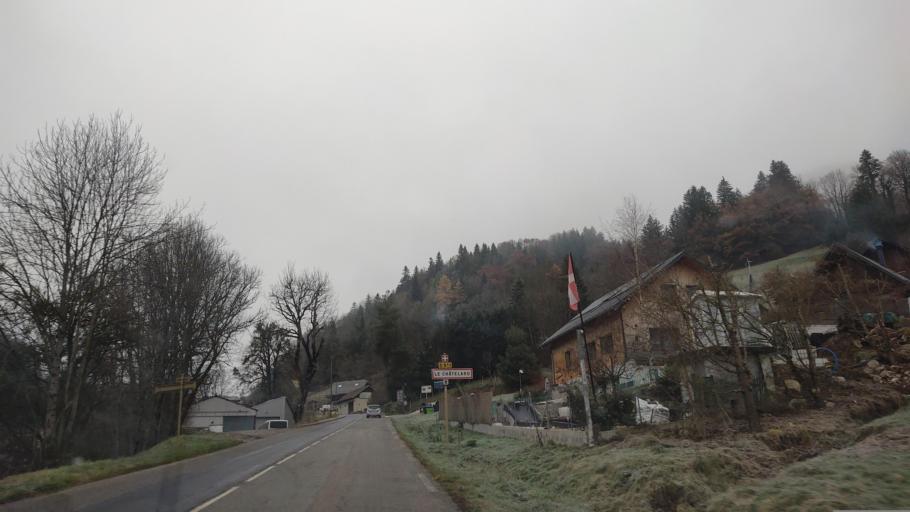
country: FR
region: Rhone-Alpes
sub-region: Departement de la Haute-Savoie
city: Doussard
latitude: 45.6782
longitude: 6.1430
